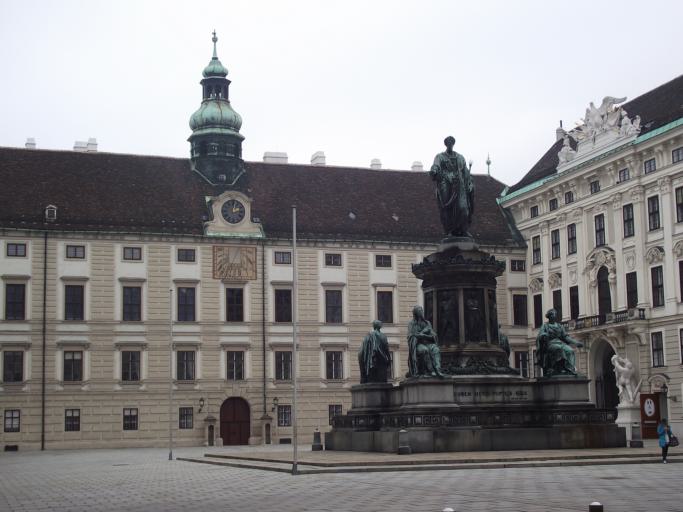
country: AT
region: Vienna
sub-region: Wien Stadt
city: Vienna
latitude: 48.2075
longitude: 16.3647
